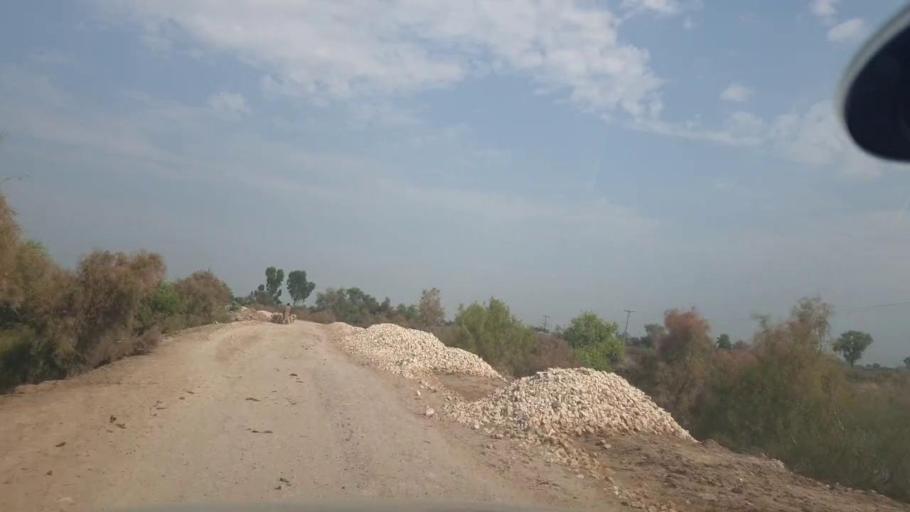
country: PK
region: Balochistan
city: Mehrabpur
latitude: 28.0713
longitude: 68.1016
